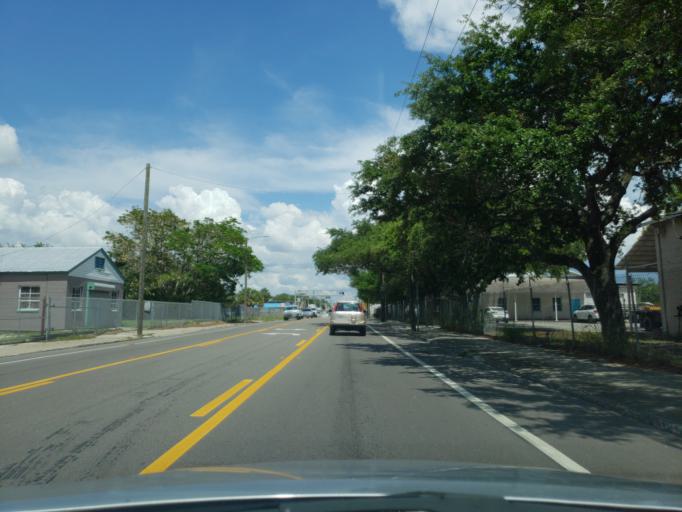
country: US
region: Florida
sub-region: Hillsborough County
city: Tampa
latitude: 27.9602
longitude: -82.4207
